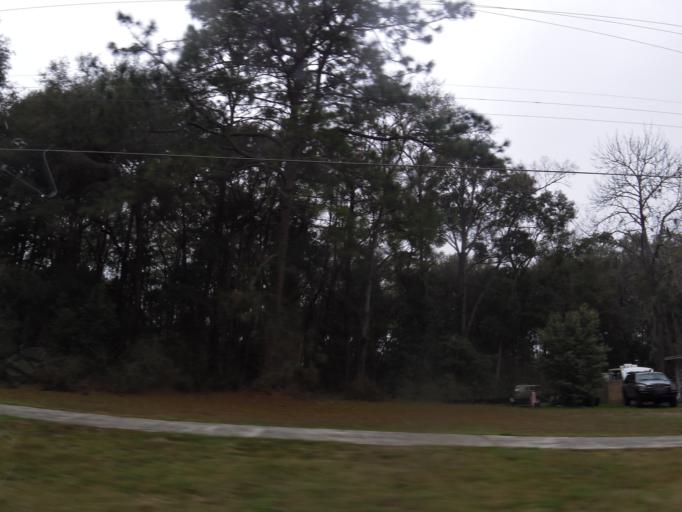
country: US
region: Florida
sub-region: Alachua County
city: High Springs
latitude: 29.8363
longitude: -82.5915
